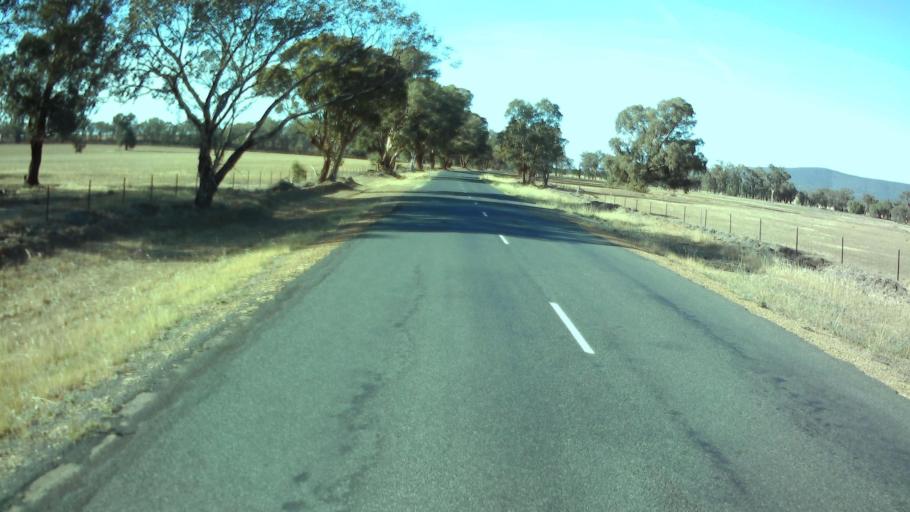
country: AU
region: New South Wales
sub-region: Weddin
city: Grenfell
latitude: -33.9371
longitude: 148.1374
